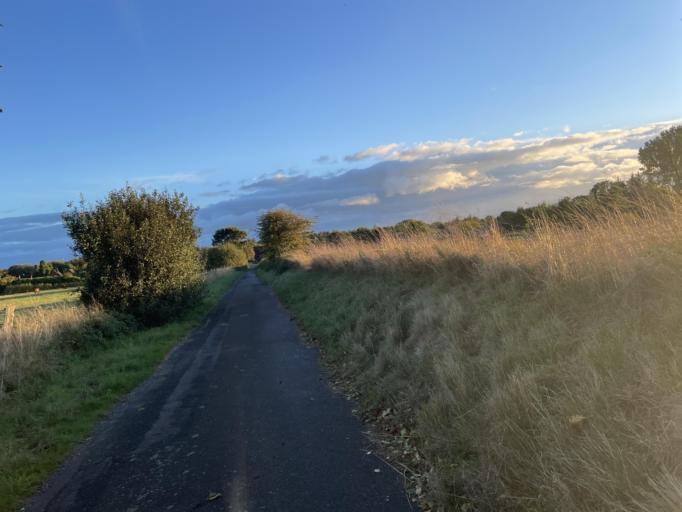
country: DE
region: Schleswig-Holstein
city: Mildstedt
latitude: 54.4795
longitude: 9.1057
